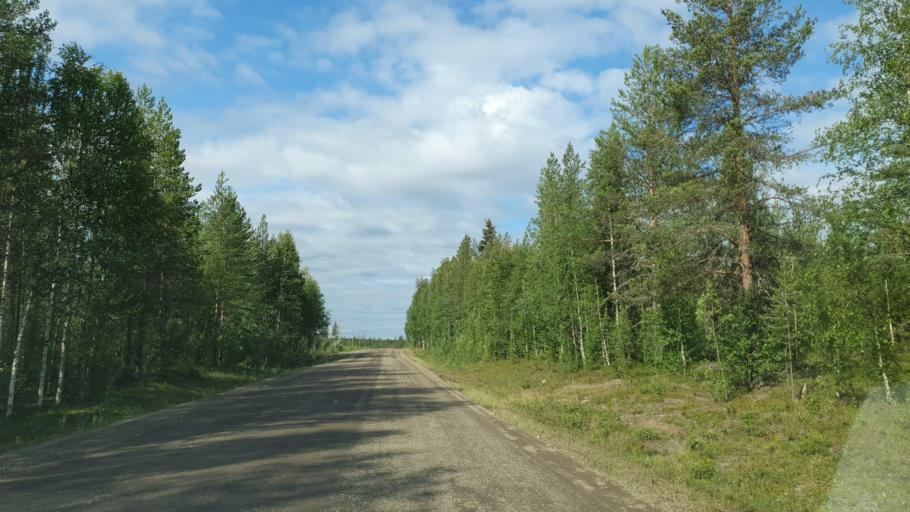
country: FI
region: Lapland
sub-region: Pohjois-Lappi
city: Sodankylae
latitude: 67.5256
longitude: 26.0044
